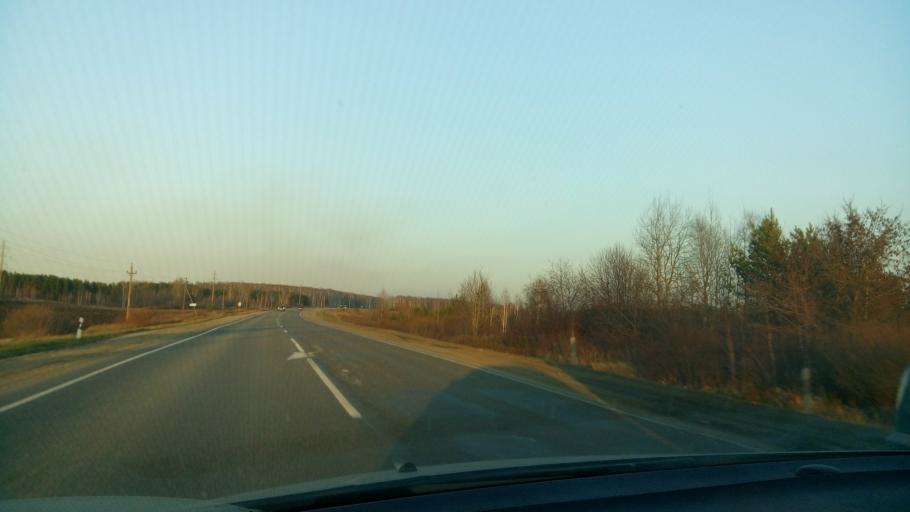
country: RU
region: Sverdlovsk
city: Obukhovskoye
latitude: 56.8525
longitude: 62.6056
